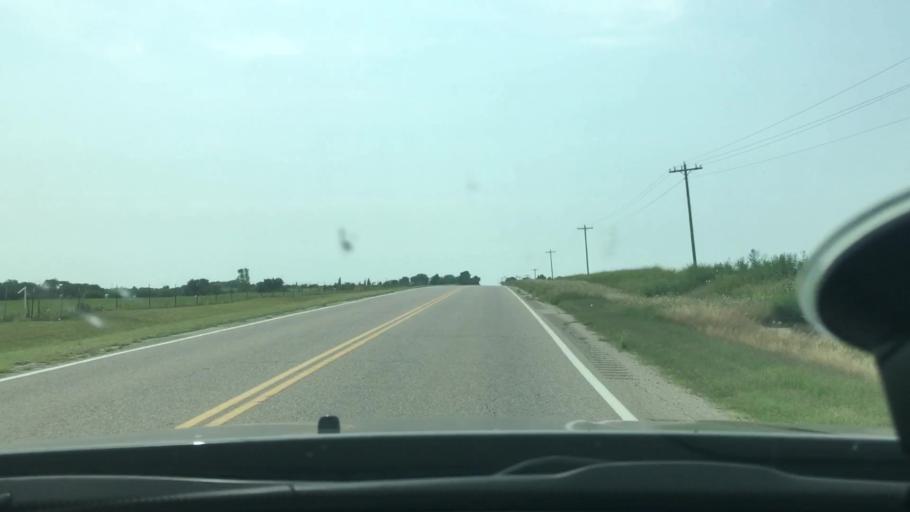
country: US
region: Oklahoma
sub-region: Marshall County
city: Madill
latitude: 34.0418
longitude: -96.7611
